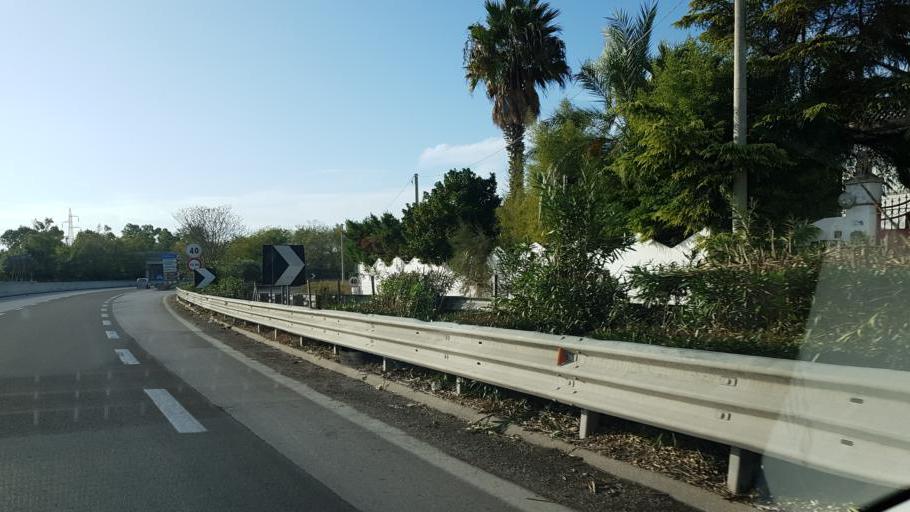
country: IT
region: Apulia
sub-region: Provincia di Brindisi
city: Francavilla Fontana
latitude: 40.5322
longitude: 17.6225
